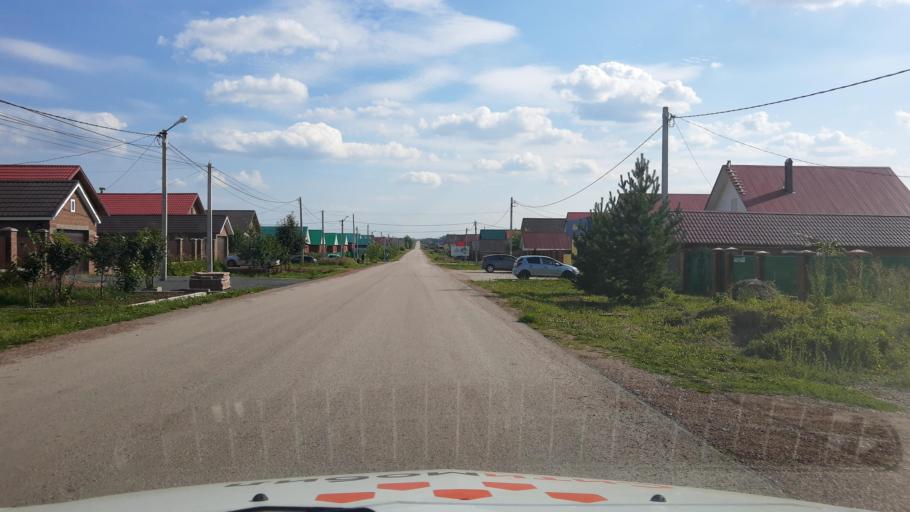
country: RU
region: Bashkortostan
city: Kabakovo
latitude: 54.6650
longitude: 56.2138
